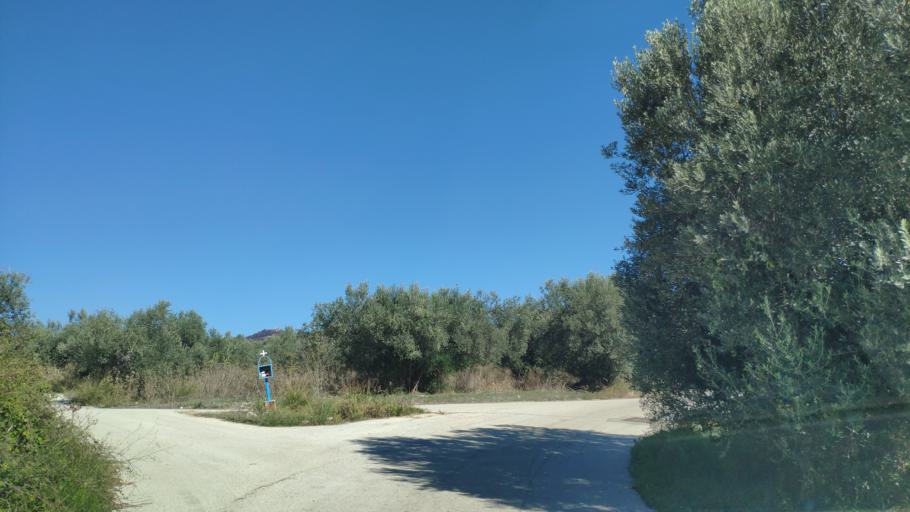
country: GR
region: Peloponnese
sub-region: Nomos Korinthias
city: Athikia
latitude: 37.8397
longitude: 22.9176
